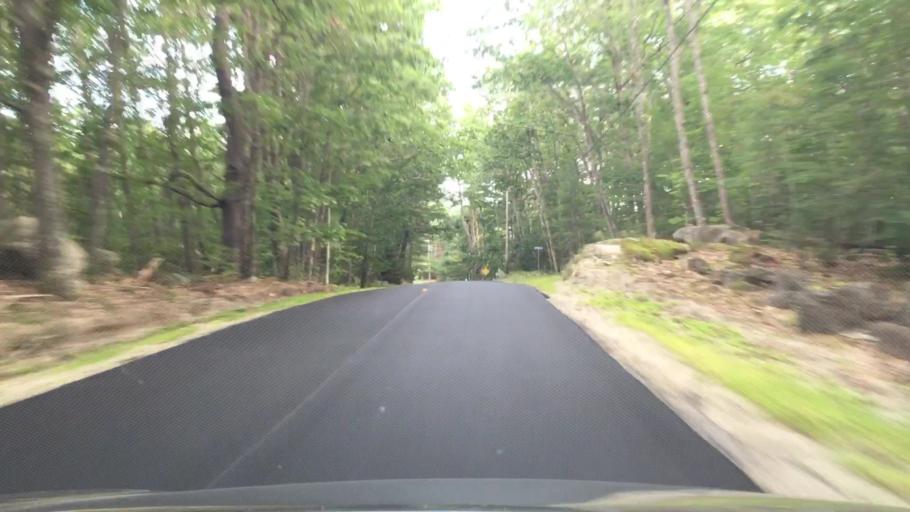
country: US
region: Maine
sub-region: Hancock County
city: Surry
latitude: 44.5201
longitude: -68.6079
